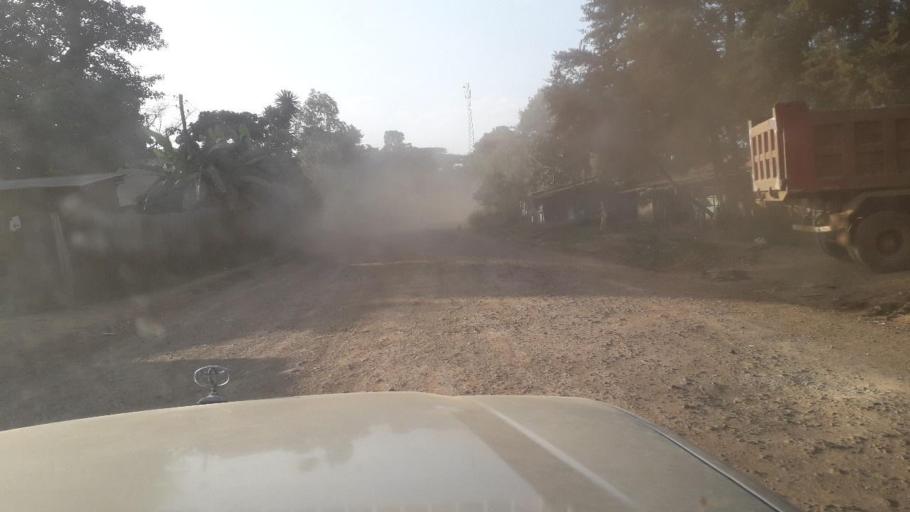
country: ET
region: Oromiya
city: Jima
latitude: 7.5985
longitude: 36.8459
